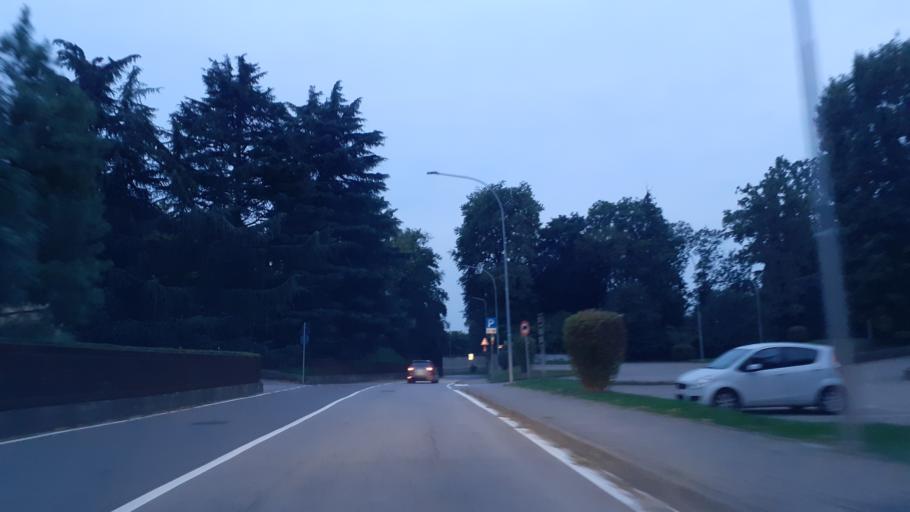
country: IT
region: Lombardy
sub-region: Provincia di Lecco
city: Bulciago
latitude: 45.7560
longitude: 9.2887
